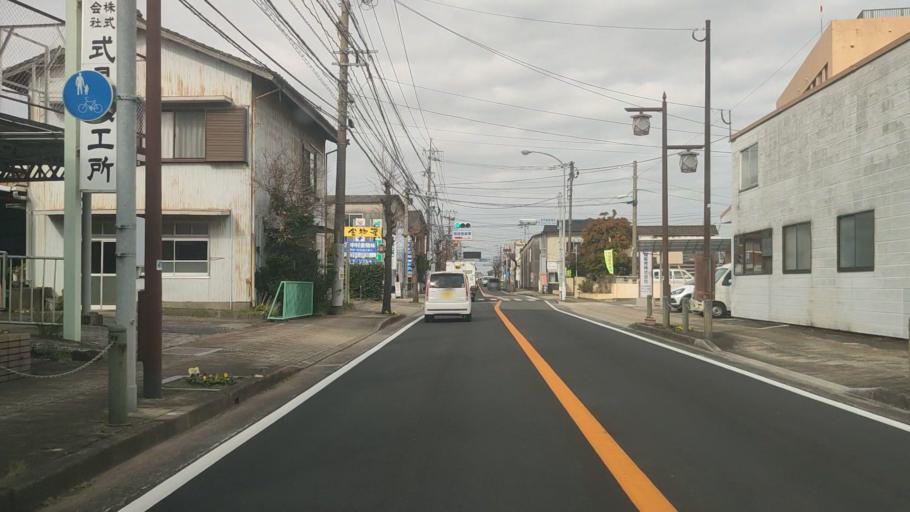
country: JP
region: Nagasaki
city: Shimabara
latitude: 32.7979
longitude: 130.3663
